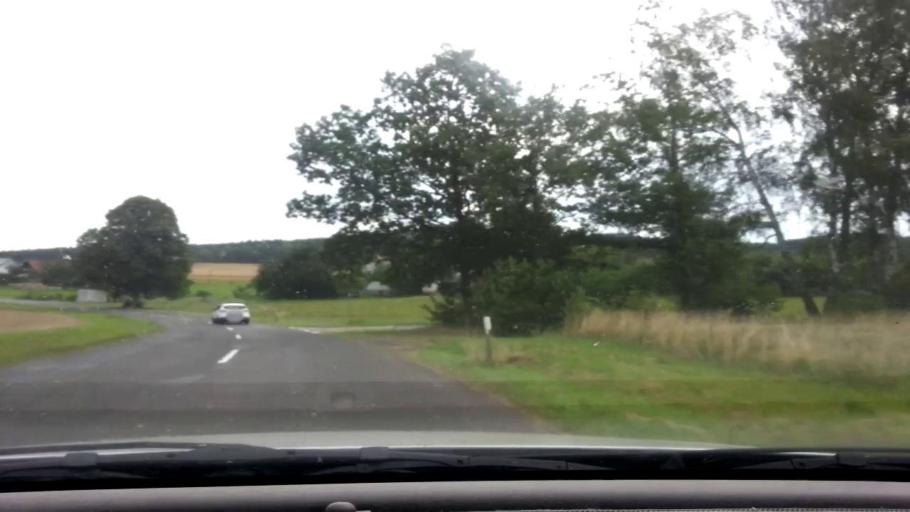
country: DE
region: Bavaria
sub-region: Upper Palatinate
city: Kulmain
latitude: 49.8773
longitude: 11.9369
